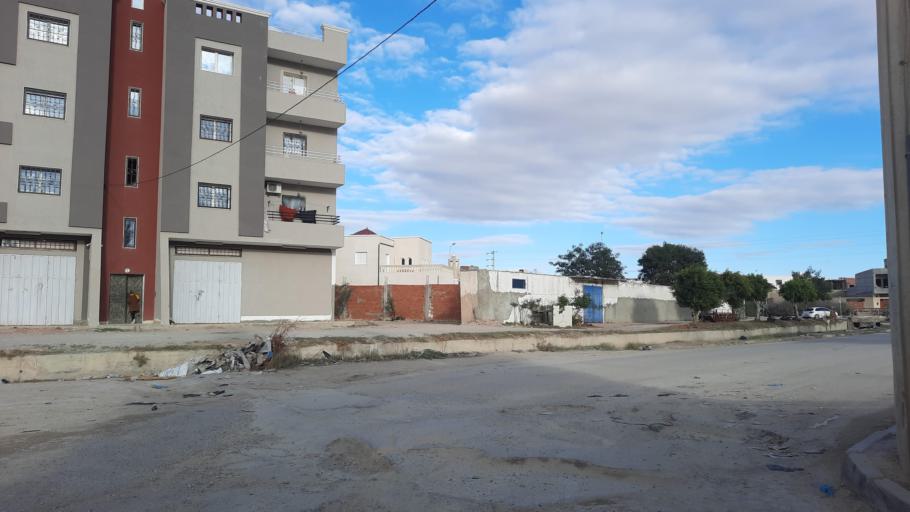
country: TN
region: Al Mahdiyah
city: El Jem
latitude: 35.2861
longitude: 10.7042
